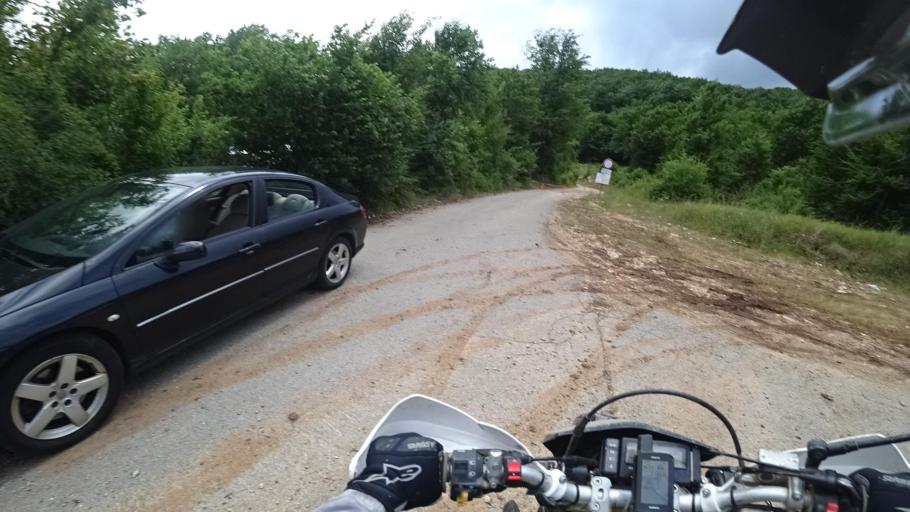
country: HR
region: Licko-Senjska
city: Jezerce
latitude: 44.7228
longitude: 15.5029
